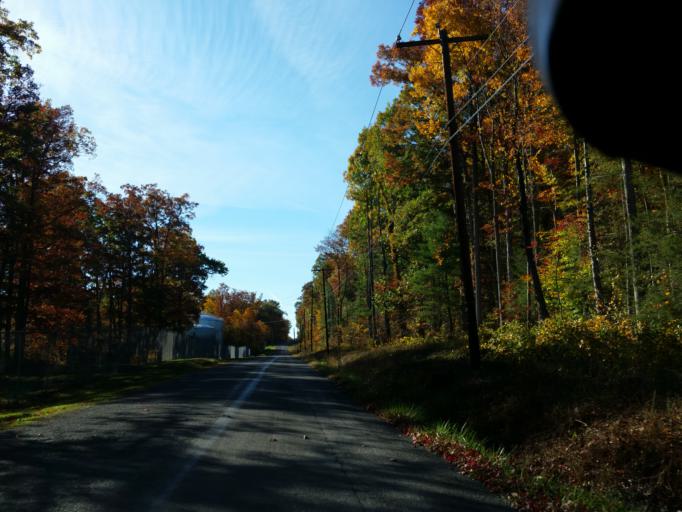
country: US
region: Pennsylvania
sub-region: Northumberland County
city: Dewart
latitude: 41.0734
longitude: -76.9598
